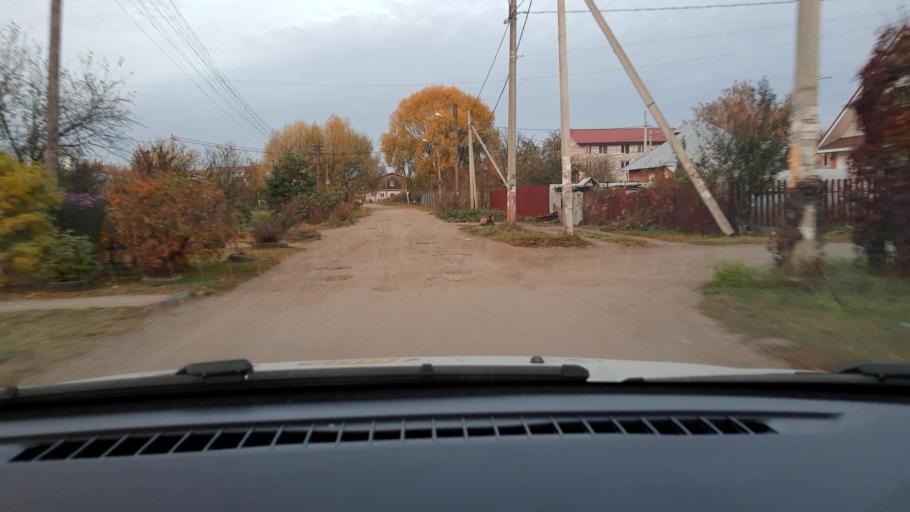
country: RU
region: Nizjnij Novgorod
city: Burevestnik
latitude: 56.2111
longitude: 43.8171
